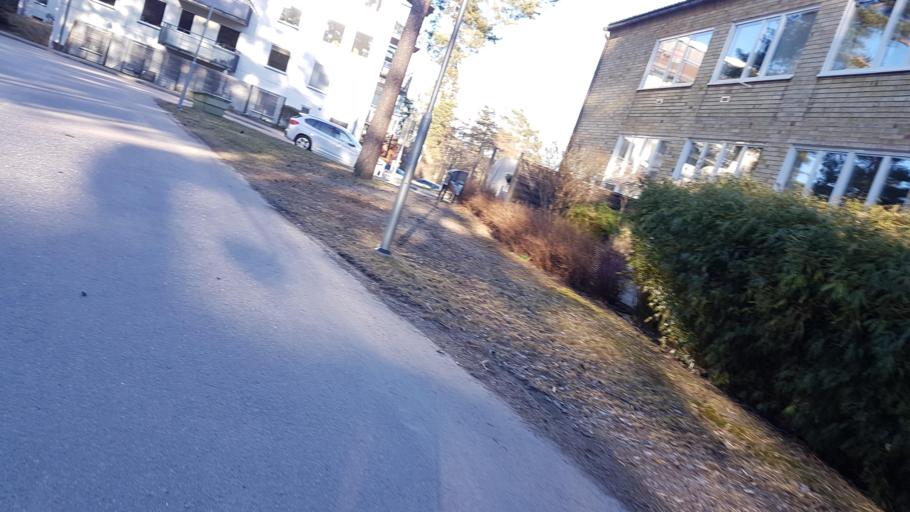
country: SE
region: Stockholm
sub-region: Stockholms Kommun
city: Arsta
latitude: 59.2662
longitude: 18.0740
